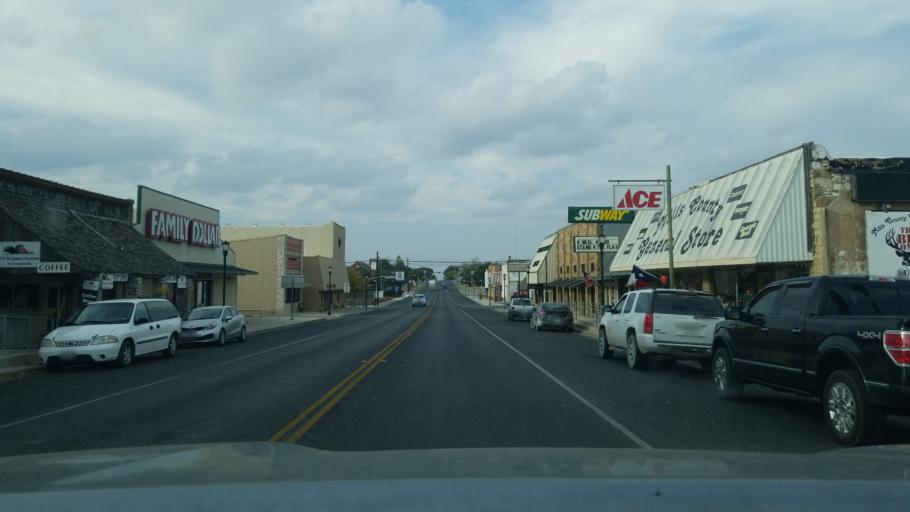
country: US
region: Texas
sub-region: Mills County
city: Goldthwaite
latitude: 31.4506
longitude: -98.5693
